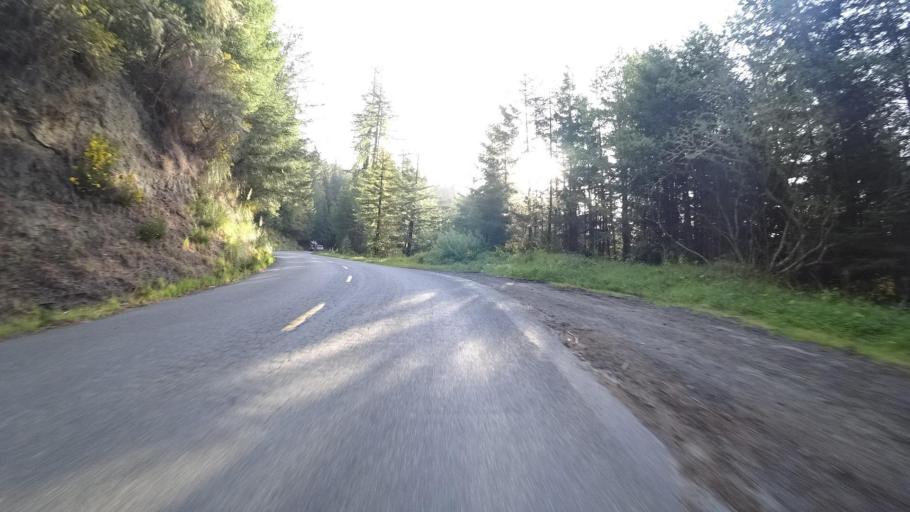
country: US
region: California
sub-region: Humboldt County
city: Bayside
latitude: 40.7551
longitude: -124.0411
